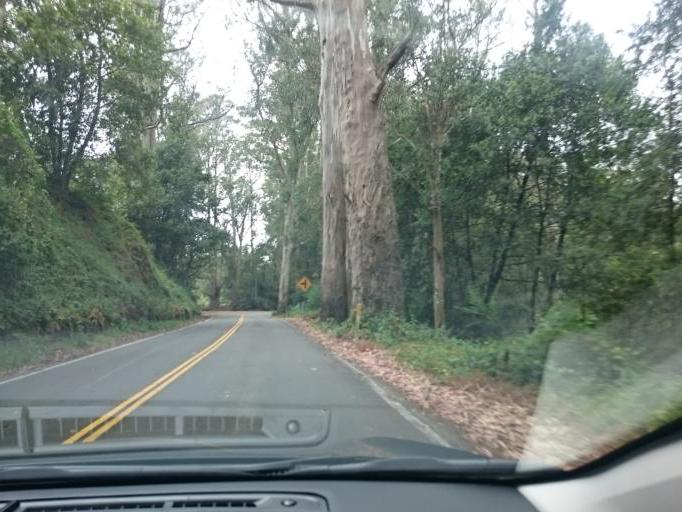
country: US
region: California
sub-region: Marin County
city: Bolinas
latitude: 37.9389
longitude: -122.7041
